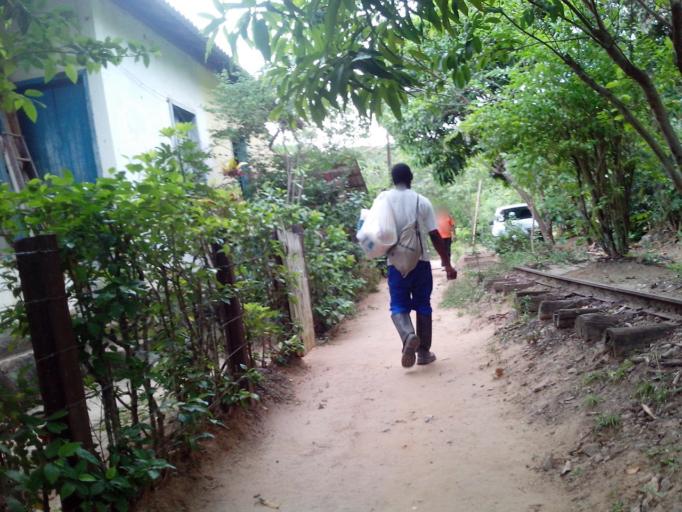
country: BR
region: Rio de Janeiro
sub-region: Miguel Pereira
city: Miguel Pereira
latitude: -22.5088
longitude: -43.5194
